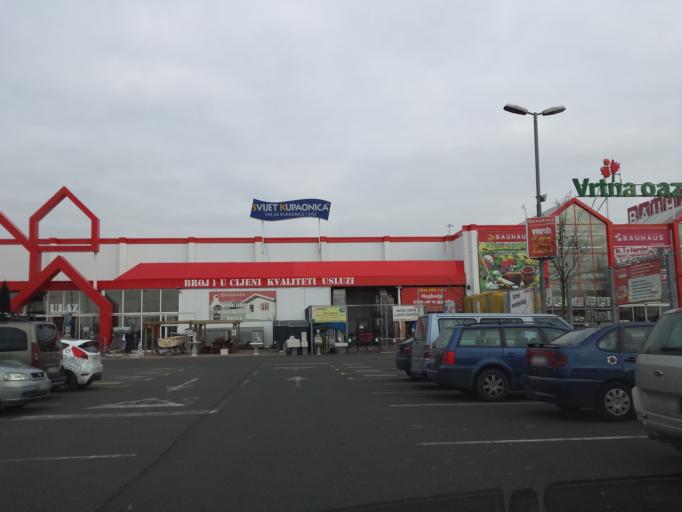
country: HR
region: Grad Zagreb
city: Jezdovec
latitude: 45.7963
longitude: 15.8620
